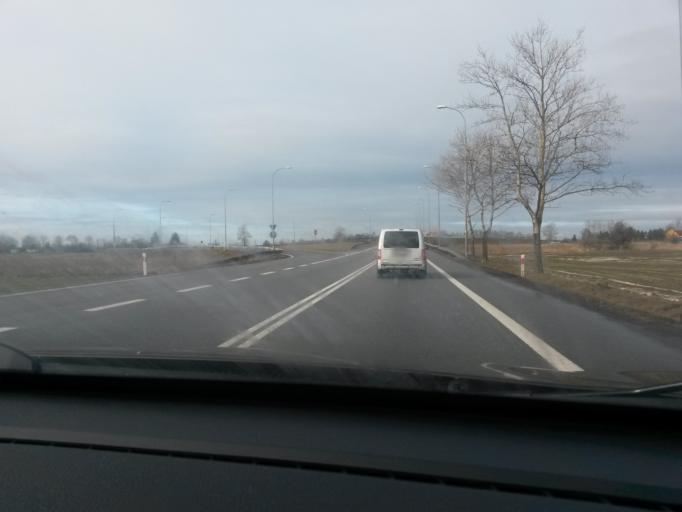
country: PL
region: Pomeranian Voivodeship
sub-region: Powiat nowodworski
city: Nowy Dwor Gdanski
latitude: 54.1981
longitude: 19.1228
